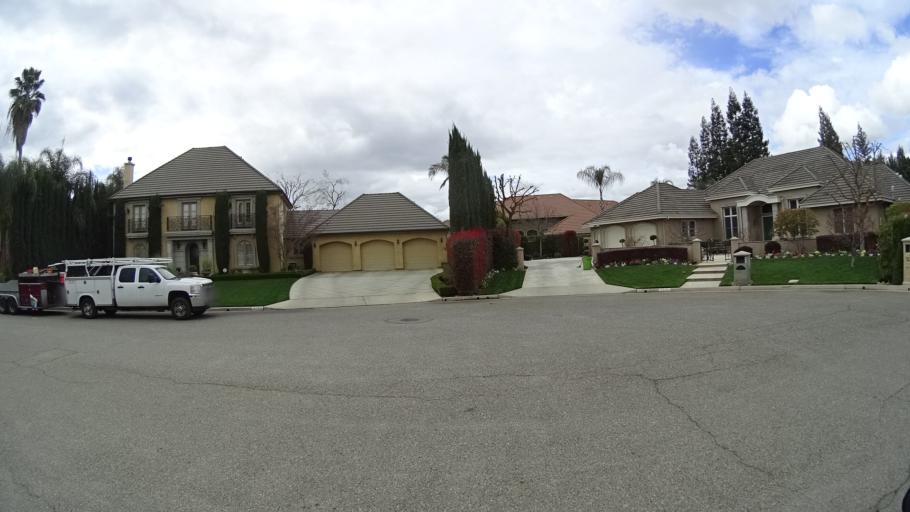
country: US
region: California
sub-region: Fresno County
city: Fresno
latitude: 36.8395
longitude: -119.8324
